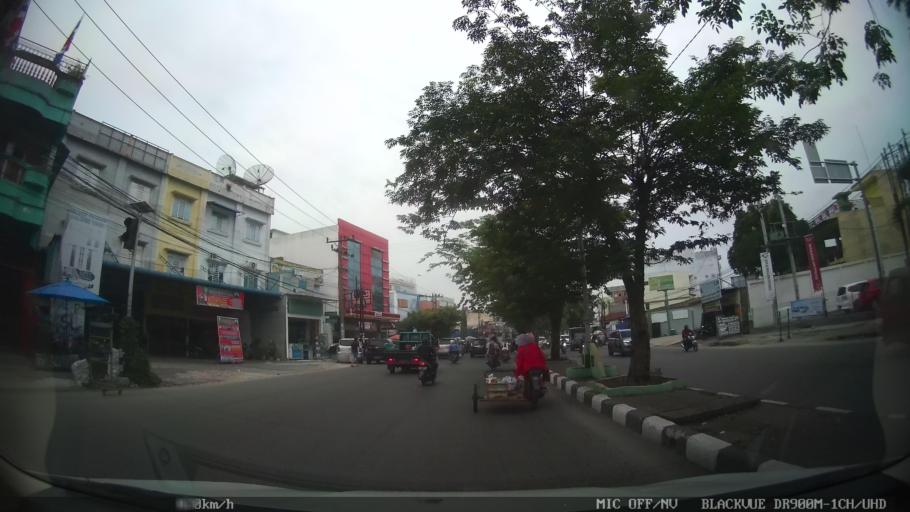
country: ID
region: North Sumatra
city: Deli Tua
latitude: 3.5505
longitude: 98.6979
